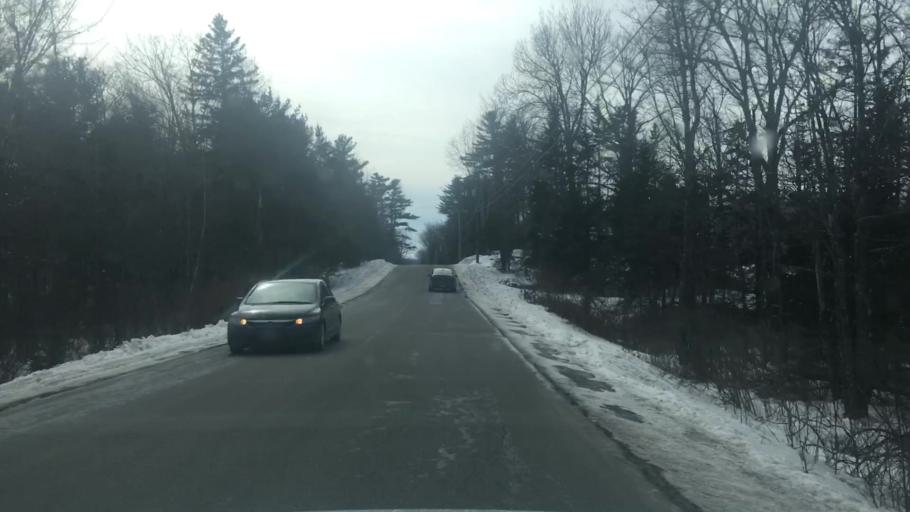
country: US
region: Maine
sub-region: Hancock County
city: Orland
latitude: 44.6036
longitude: -68.7191
